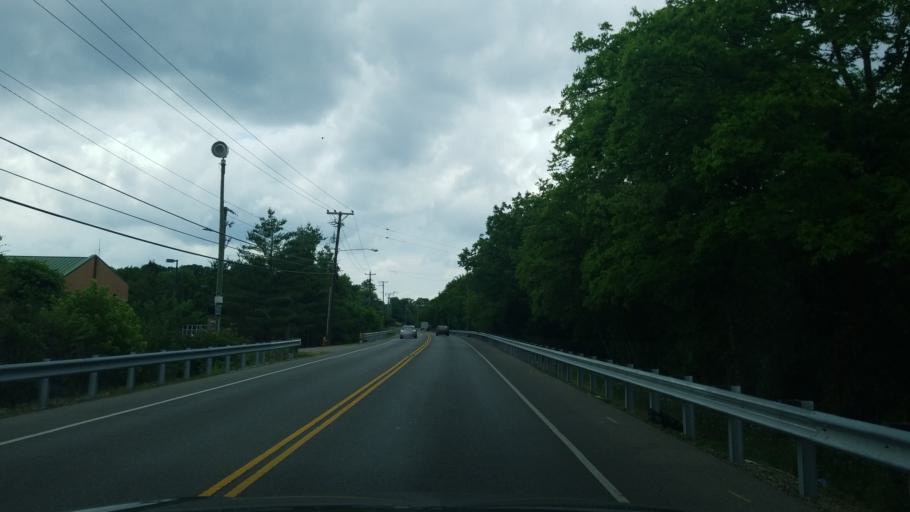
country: US
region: Tennessee
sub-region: Rutherford County
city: La Vergne
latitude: 36.0895
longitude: -86.6195
